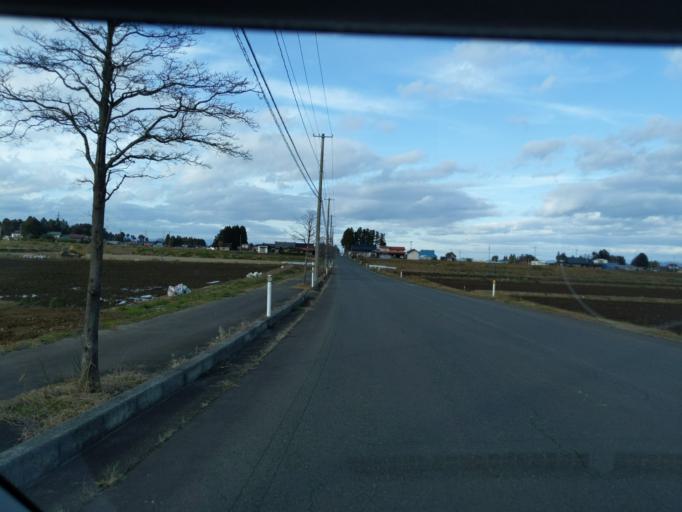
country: JP
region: Iwate
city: Mizusawa
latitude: 39.1201
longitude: 141.0926
